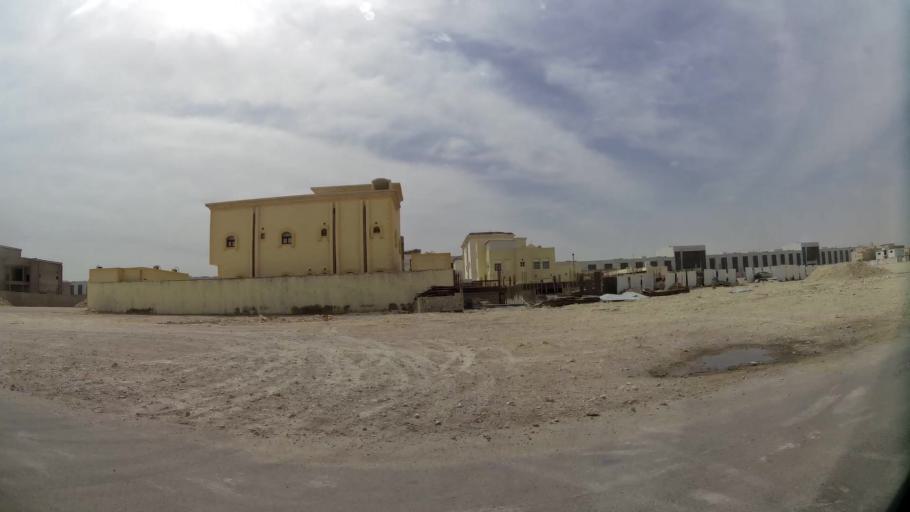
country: QA
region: Al Wakrah
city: Al Wukayr
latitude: 25.2016
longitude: 51.4680
